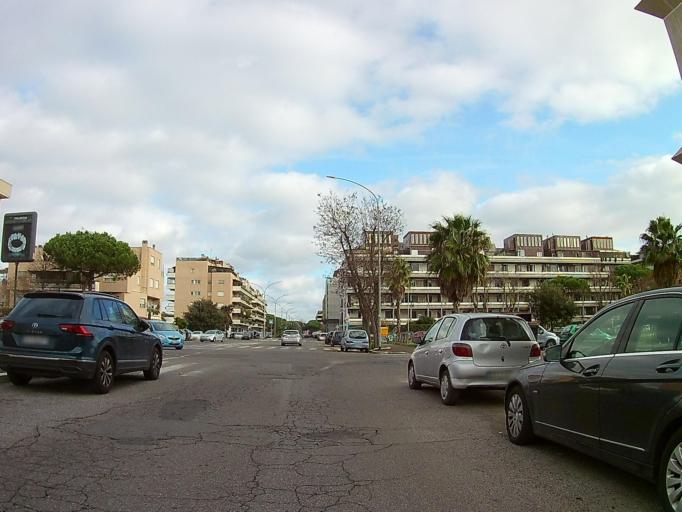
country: IT
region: Latium
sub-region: Citta metropolitana di Roma Capitale
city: Lido di Ostia
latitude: 41.7401
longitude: 12.2673
